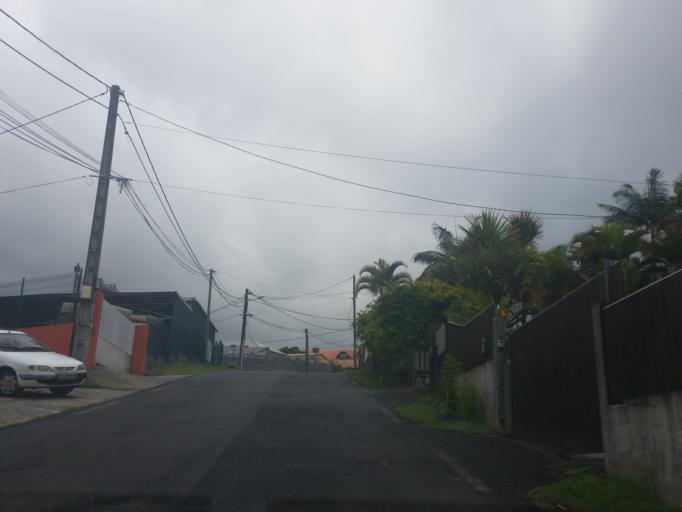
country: RE
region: Reunion
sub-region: Reunion
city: Le Tampon
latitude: -21.2436
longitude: 55.5128
